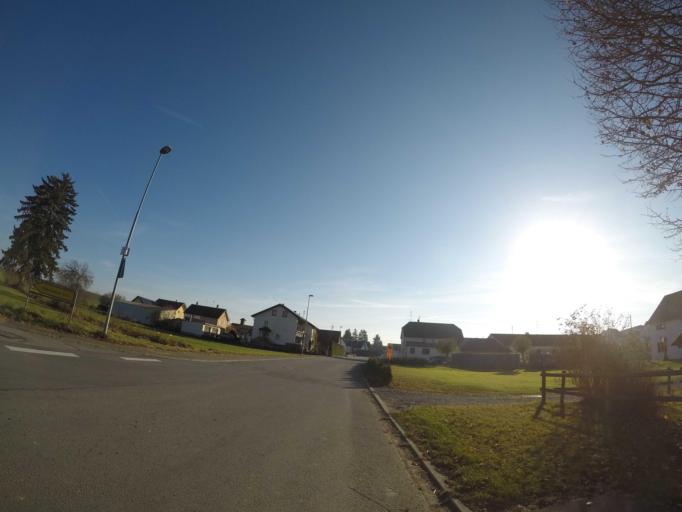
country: DE
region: Baden-Wuerttemberg
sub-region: Tuebingen Region
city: Grundsheim
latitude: 48.1773
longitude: 9.6677
